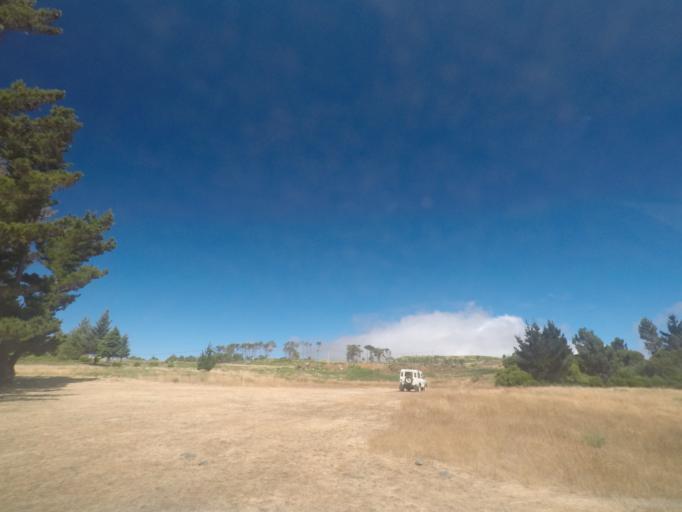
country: PT
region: Madeira
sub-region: Funchal
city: Nossa Senhora do Monte
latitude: 32.7120
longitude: -16.9074
